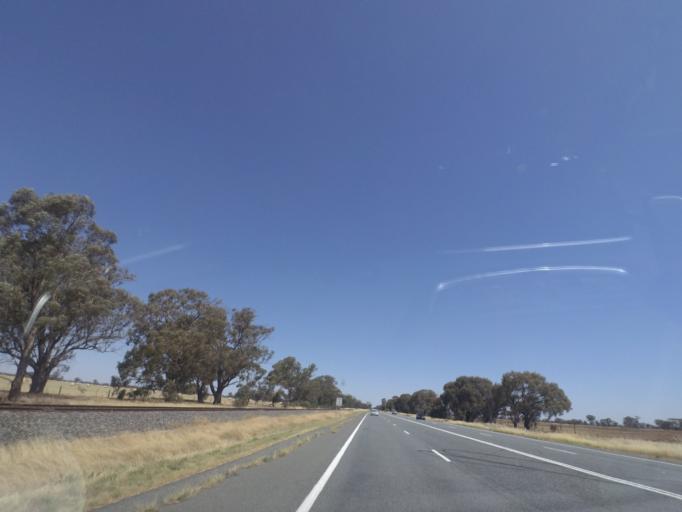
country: AU
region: Victoria
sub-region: Greater Shepparton
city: Shepparton
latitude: -36.1934
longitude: 145.4319
